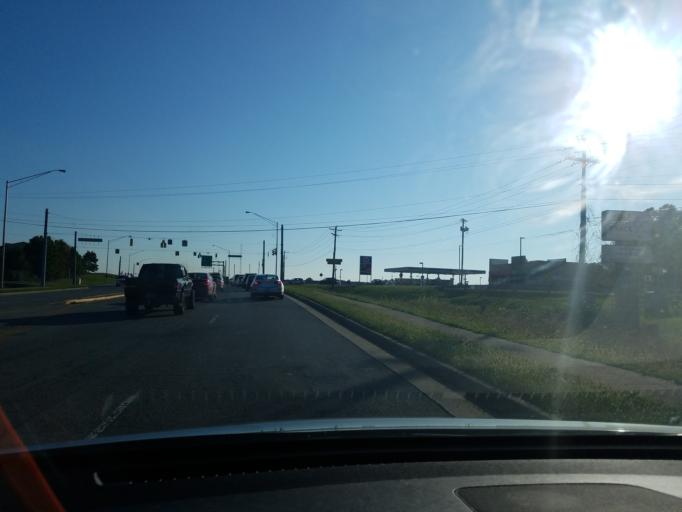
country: US
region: Indiana
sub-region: Clark County
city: Clarksville
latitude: 38.3475
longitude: -85.7975
